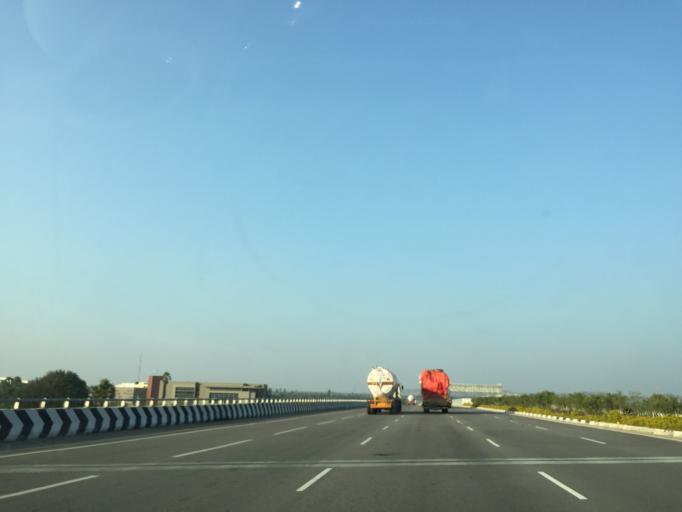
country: IN
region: Telangana
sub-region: Rangareddi
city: Ghatkesar
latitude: 17.4515
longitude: 78.6682
